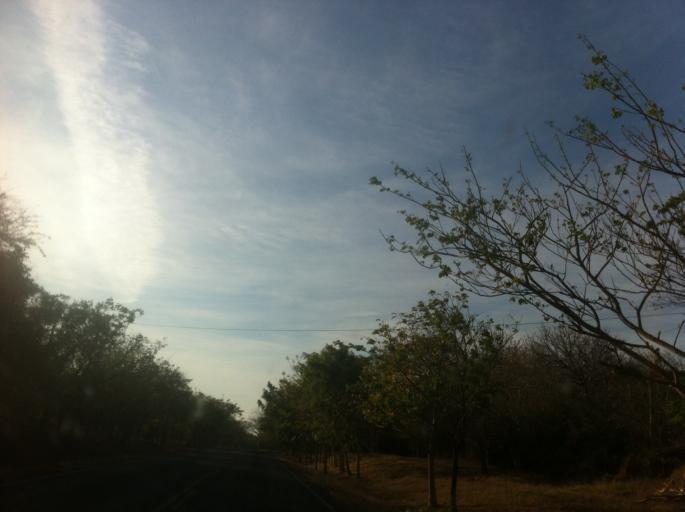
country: NI
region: Rivas
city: San Jorge
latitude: 11.3224
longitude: -85.7134
